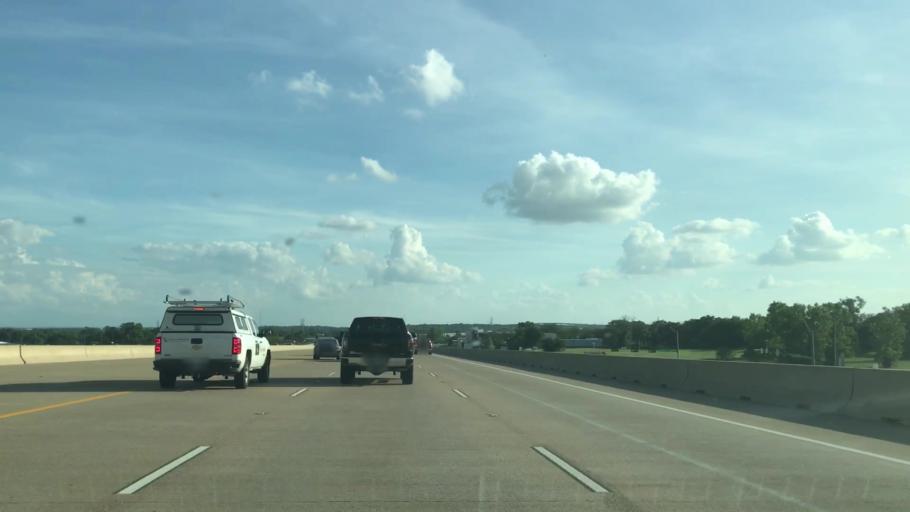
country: US
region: Texas
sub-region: Dallas County
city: Grand Prairie
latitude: 32.8005
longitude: -97.0187
